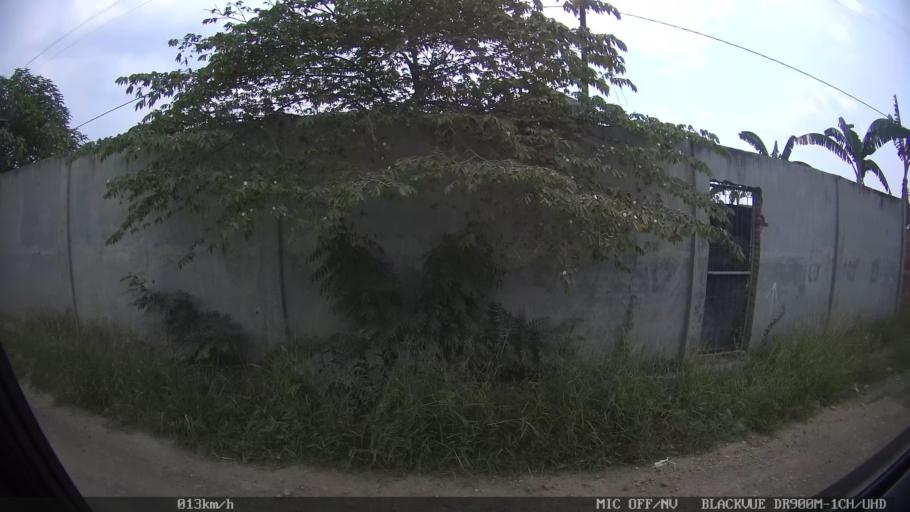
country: ID
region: Lampung
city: Gadingrejo
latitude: -5.3735
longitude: 105.0289
